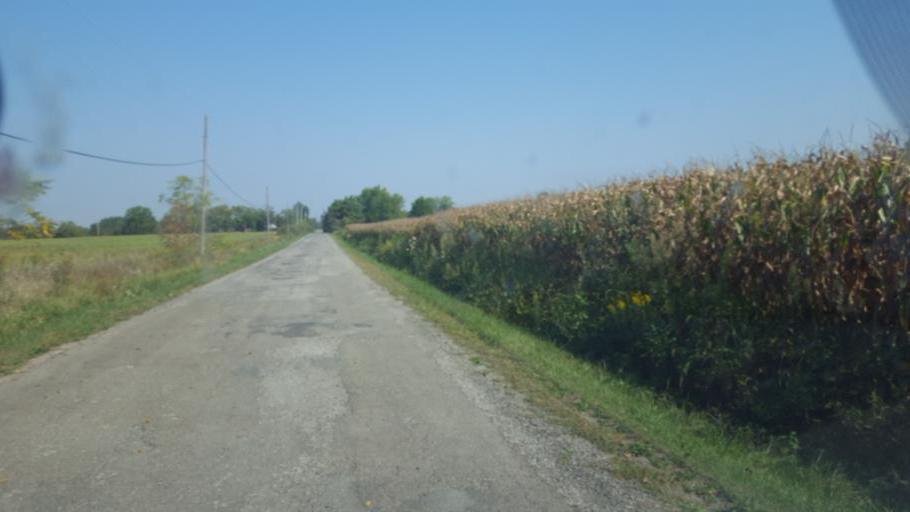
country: US
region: Ohio
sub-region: Crawford County
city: Galion
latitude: 40.6629
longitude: -82.7940
